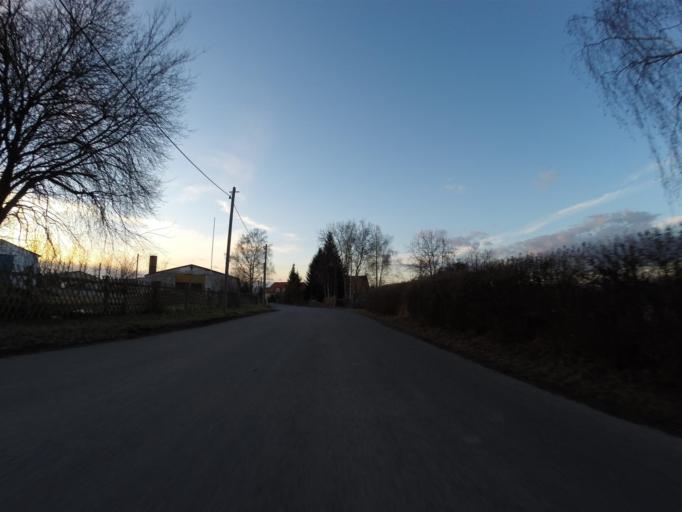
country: DE
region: Thuringia
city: Apolda
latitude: 50.9996
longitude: 11.5246
